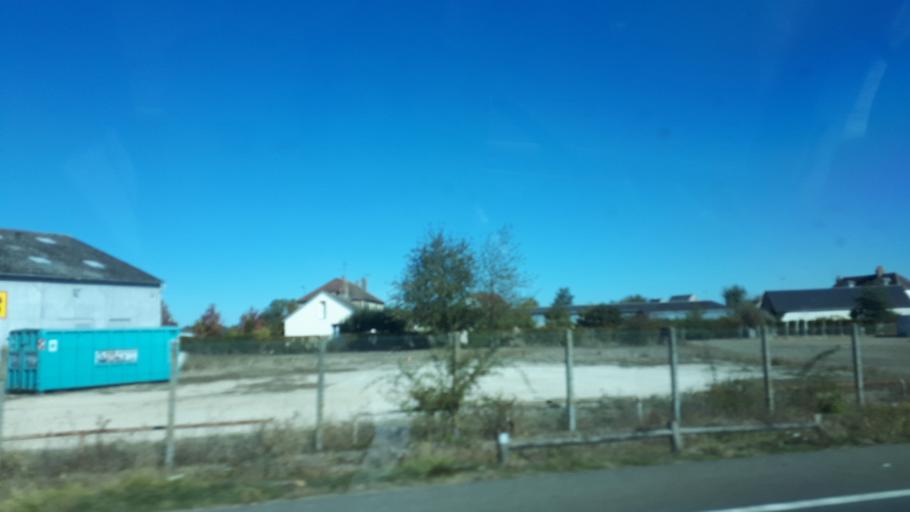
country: FR
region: Centre
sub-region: Departement d'Eure-et-Loir
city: Chateaudun
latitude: 48.0609
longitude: 1.3318
